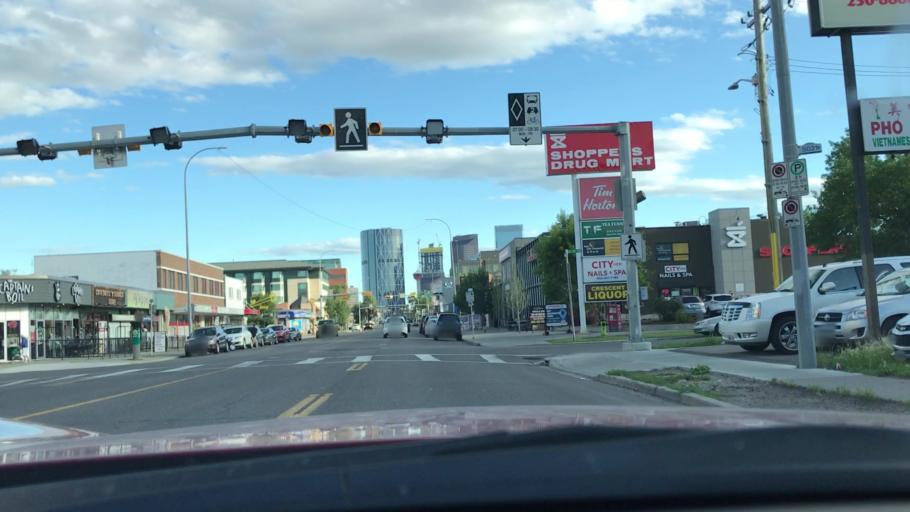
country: CA
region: Alberta
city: Calgary
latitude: 51.0648
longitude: -114.0626
